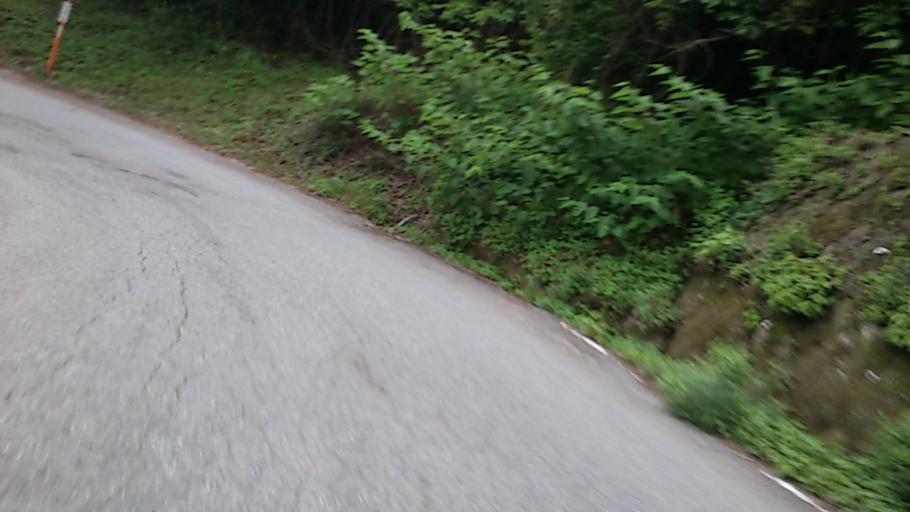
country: JP
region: Nagano
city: Saku
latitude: 36.2260
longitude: 138.6190
